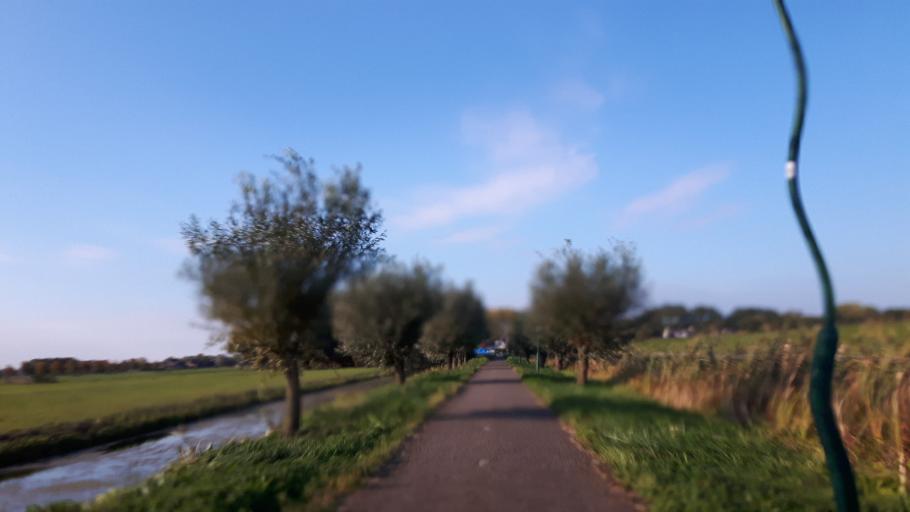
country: NL
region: Utrecht
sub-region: Gemeente Oudewater
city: Oudewater
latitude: 52.0137
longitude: 4.8813
